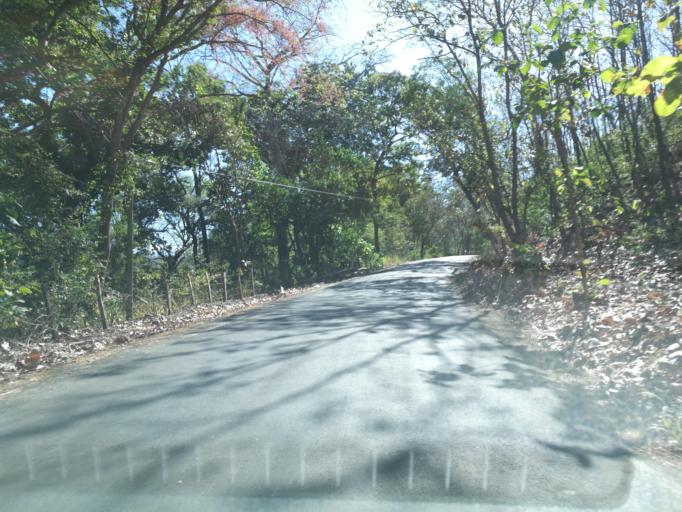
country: CR
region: Puntarenas
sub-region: Canton Central de Puntarenas
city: Puntarenas
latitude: 10.0885
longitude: -84.9423
